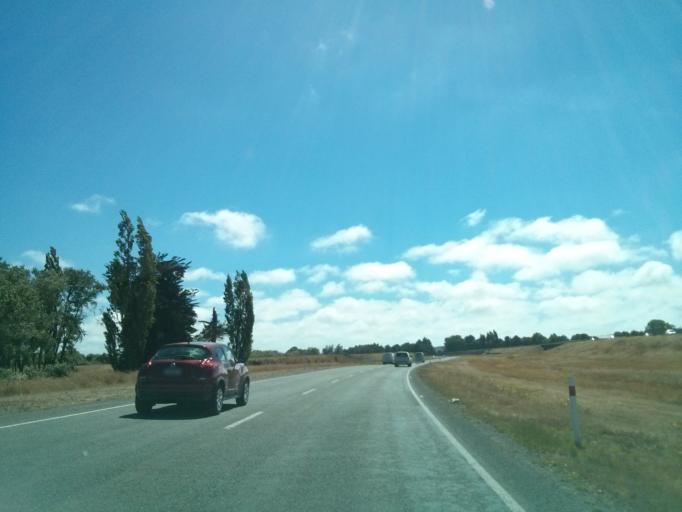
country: NZ
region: Canterbury
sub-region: Waimakariri District
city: Kaiapoi
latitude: -43.4323
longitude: 172.6412
